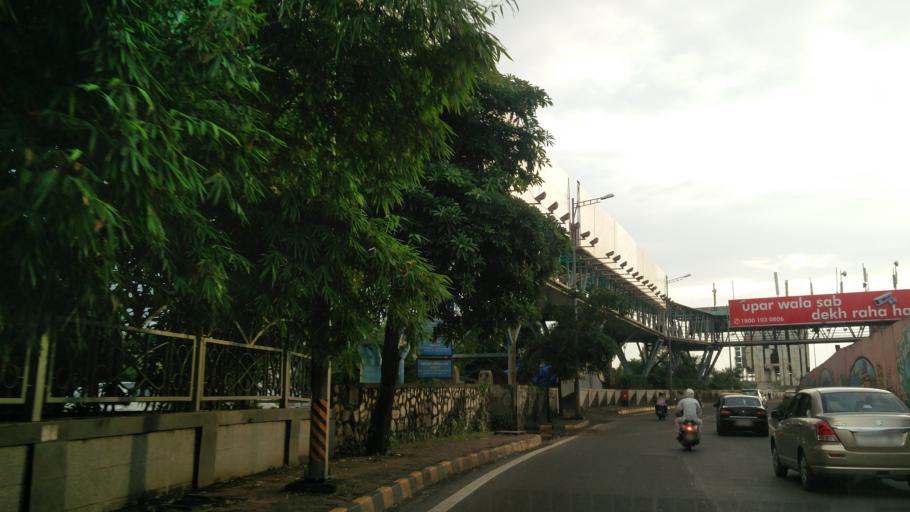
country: IN
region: Maharashtra
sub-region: Mumbai Suburban
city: Mumbai
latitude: 19.0530
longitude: 72.8458
